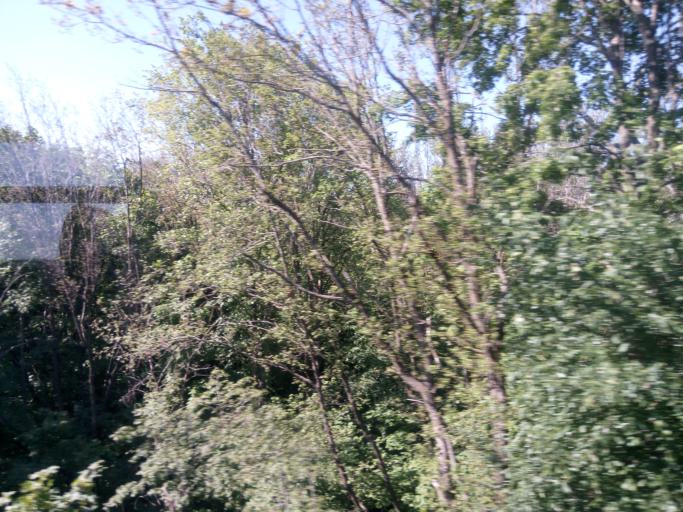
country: RU
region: Tatarstan
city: Stolbishchi
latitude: 55.6132
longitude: 49.2893
